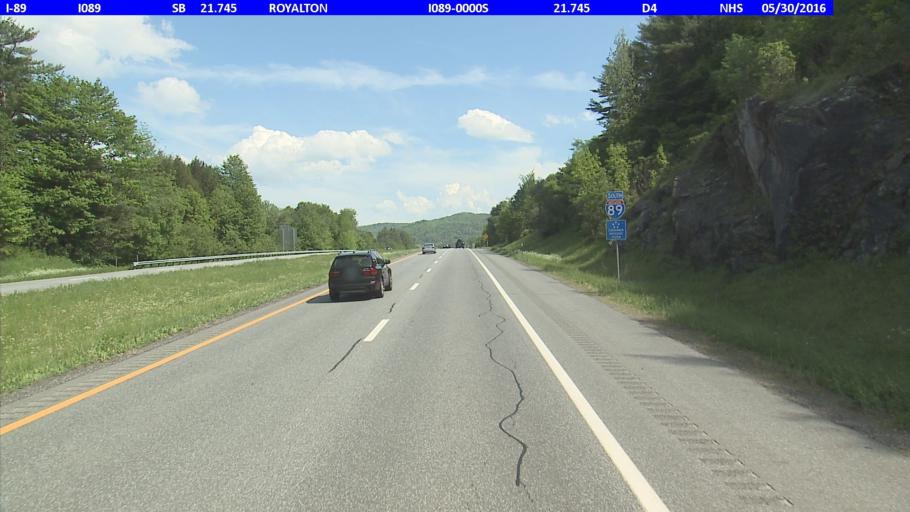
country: US
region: Vermont
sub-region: Orange County
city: Randolph
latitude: 43.8219
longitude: -72.5745
